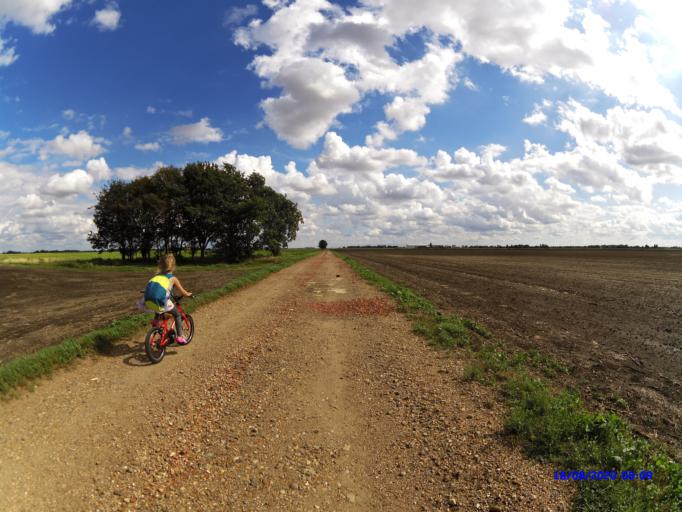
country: GB
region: England
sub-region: Cambridgeshire
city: Whittlesey
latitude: 52.5118
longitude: -0.0827
